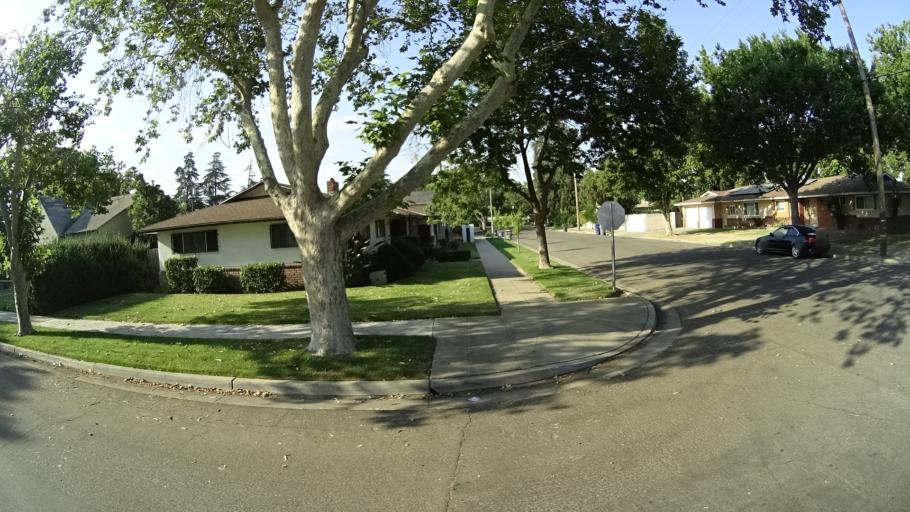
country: US
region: California
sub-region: Fresno County
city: West Park
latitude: 36.7254
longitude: -119.8116
